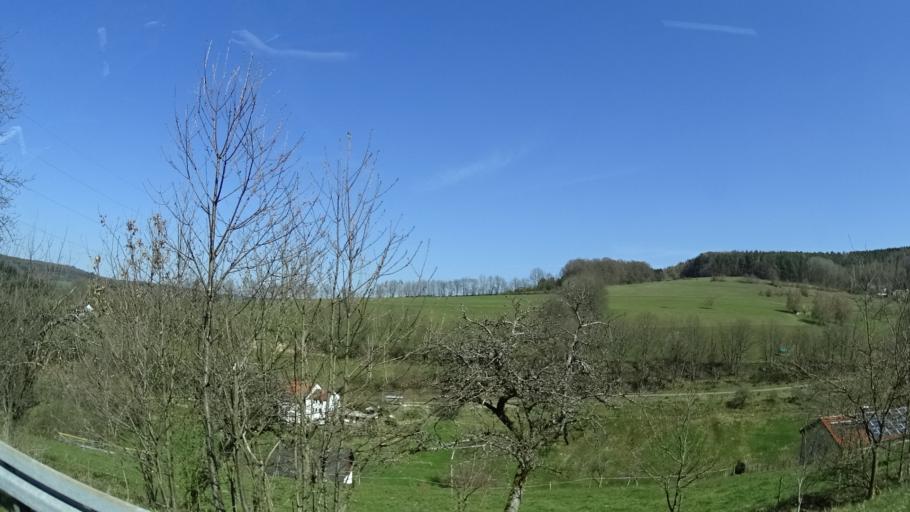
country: DE
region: Hesse
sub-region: Regierungsbezirk Darmstadt
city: Beerfelden
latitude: 49.5505
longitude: 8.9345
